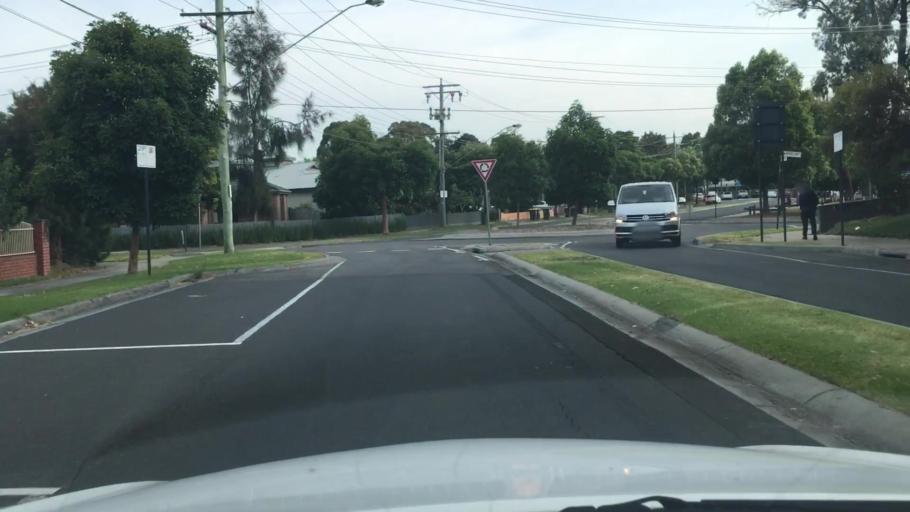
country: AU
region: Victoria
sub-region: Monash
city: Notting Hill
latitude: -37.8810
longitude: 145.1607
